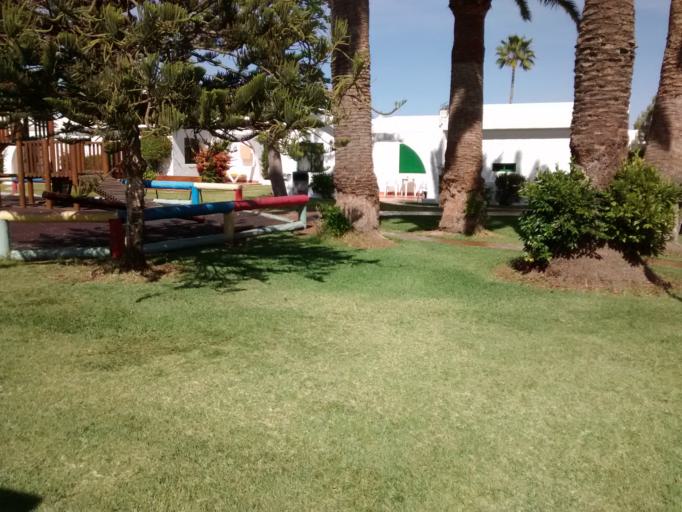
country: ES
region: Canary Islands
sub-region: Provincia de Las Palmas
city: Maspalomas
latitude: 27.7573
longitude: -15.5964
